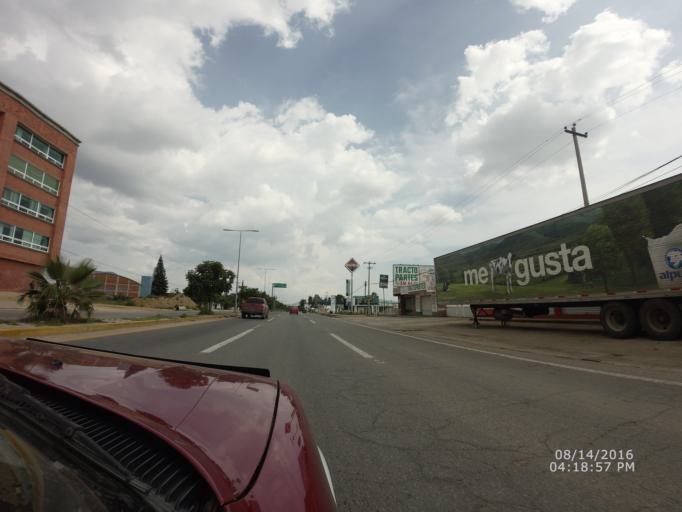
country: MX
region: Oaxaca
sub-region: San Lorenzo Cacaotepec
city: Santiago Etla
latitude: 17.1415
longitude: -96.7773
